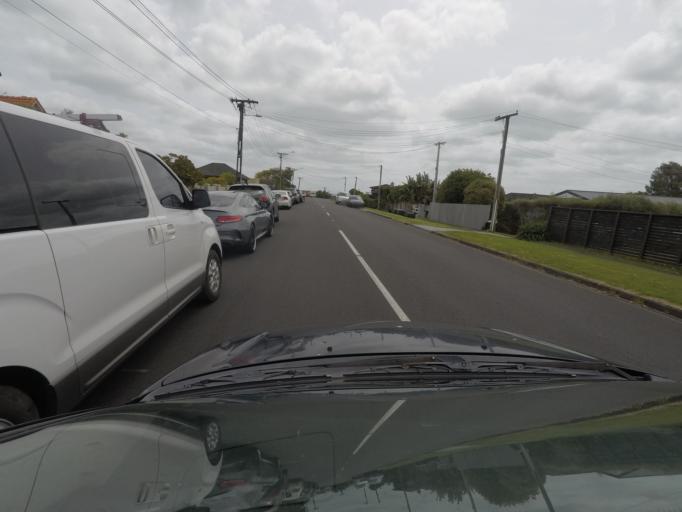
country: NZ
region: Auckland
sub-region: Auckland
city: Pakuranga
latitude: -36.8904
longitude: 174.9303
